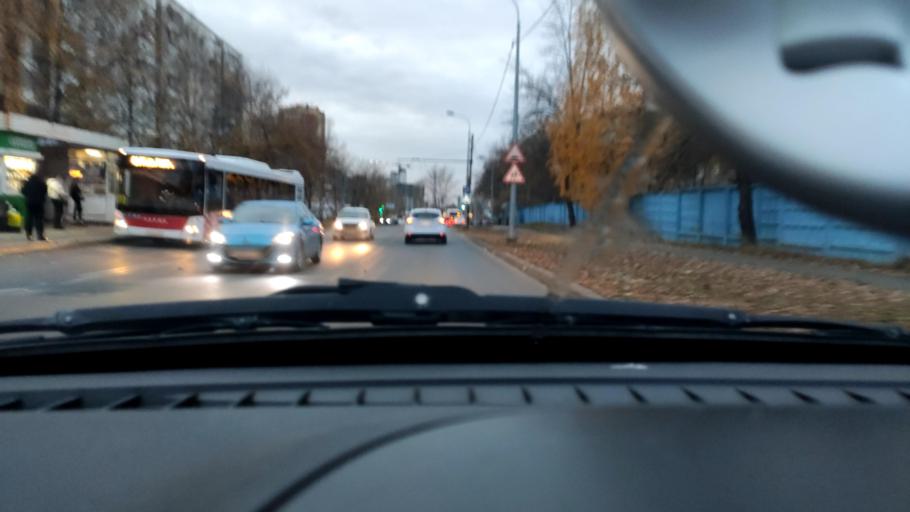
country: RU
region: Perm
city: Kondratovo
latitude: 57.9998
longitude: 56.1703
